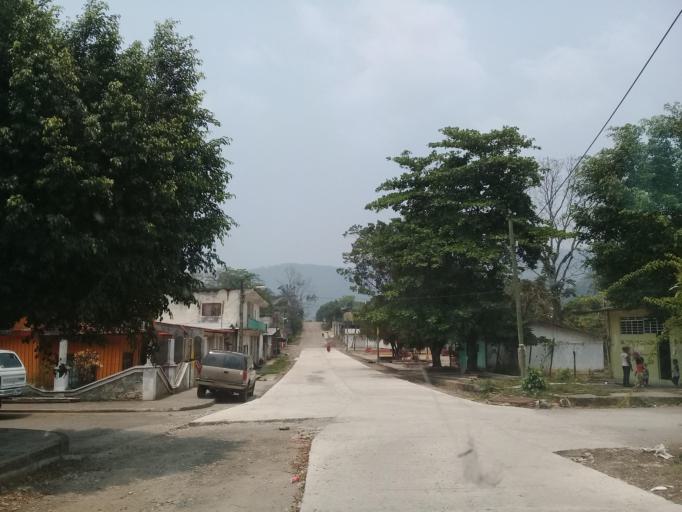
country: MX
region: Veracruz
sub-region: Tezonapa
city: Laguna Chica (Pueblo Nuevo)
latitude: 18.5445
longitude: -96.7361
